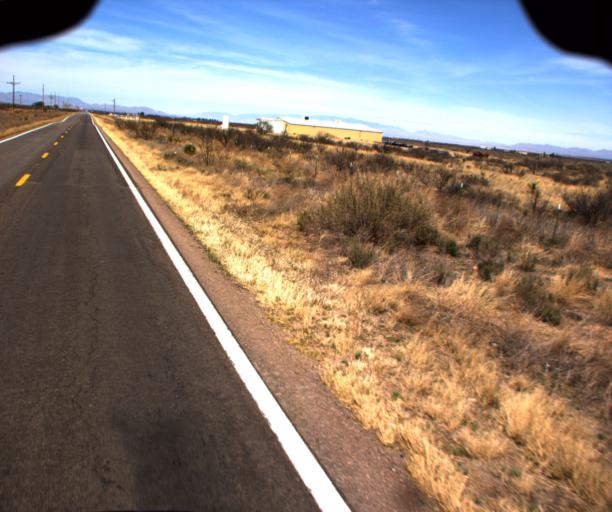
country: US
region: Arizona
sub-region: Cochise County
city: Willcox
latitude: 31.9948
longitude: -109.8583
